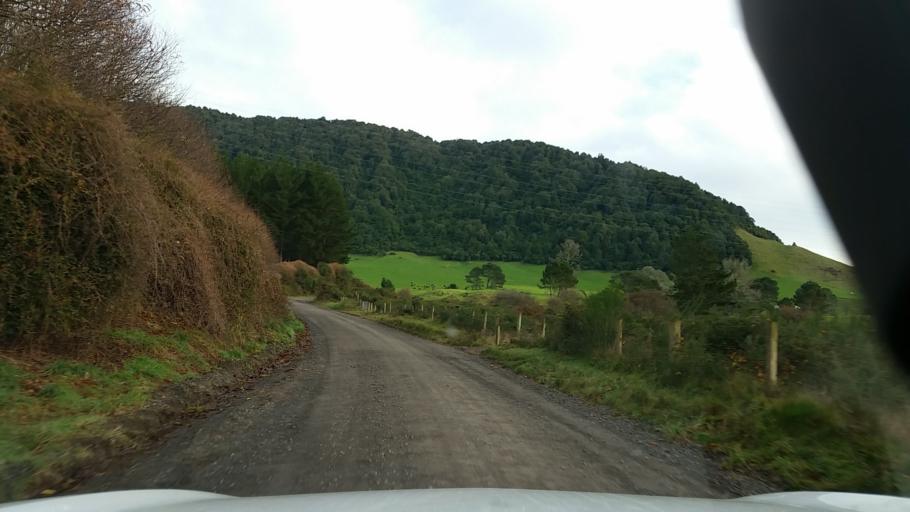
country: NZ
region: Bay of Plenty
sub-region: Rotorua District
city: Rotorua
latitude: -38.2348
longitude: 176.1647
